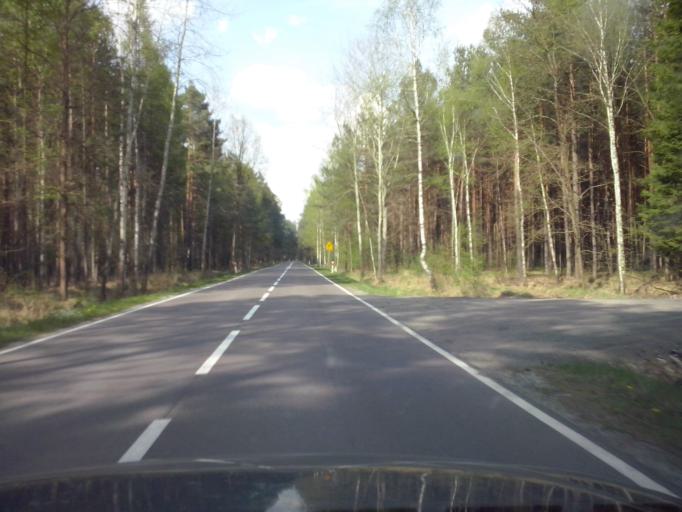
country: PL
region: Subcarpathian Voivodeship
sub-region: Powiat nizanski
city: Rudnik nad Sanem
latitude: 50.3844
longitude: 22.2620
